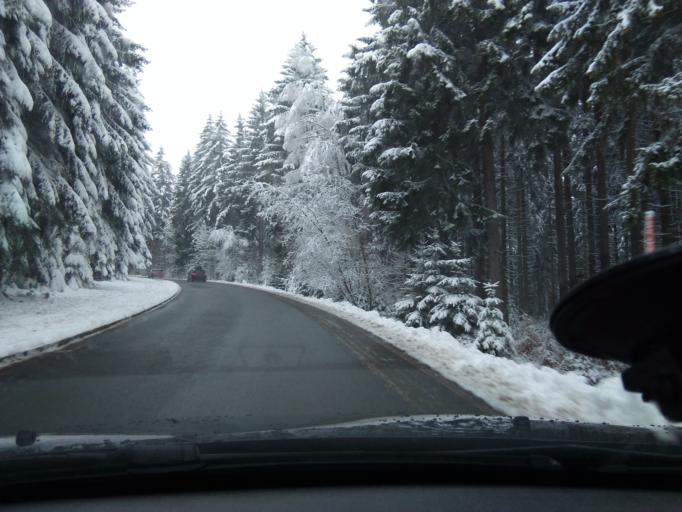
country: DE
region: Saxony
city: Markersbach
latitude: 50.5213
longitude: 12.8633
